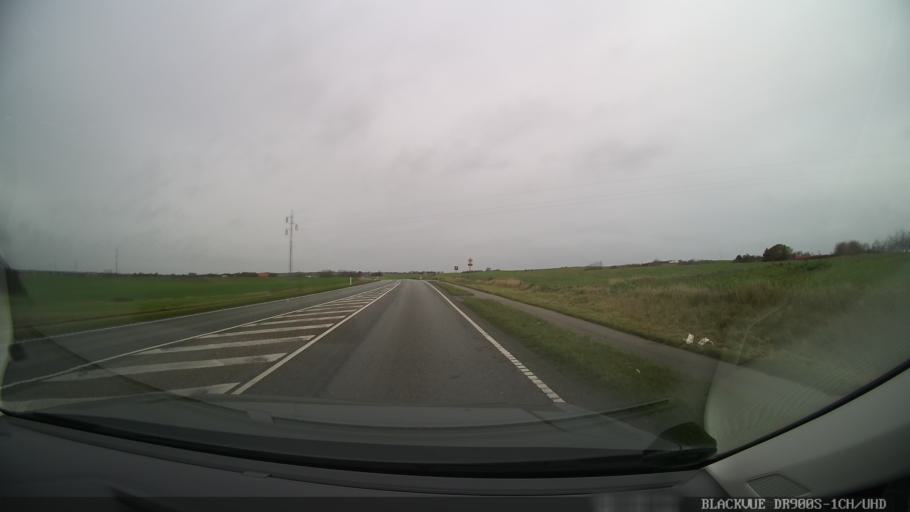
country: DK
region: North Denmark
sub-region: Thisted Kommune
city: Thisted
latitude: 56.8559
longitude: 8.6964
